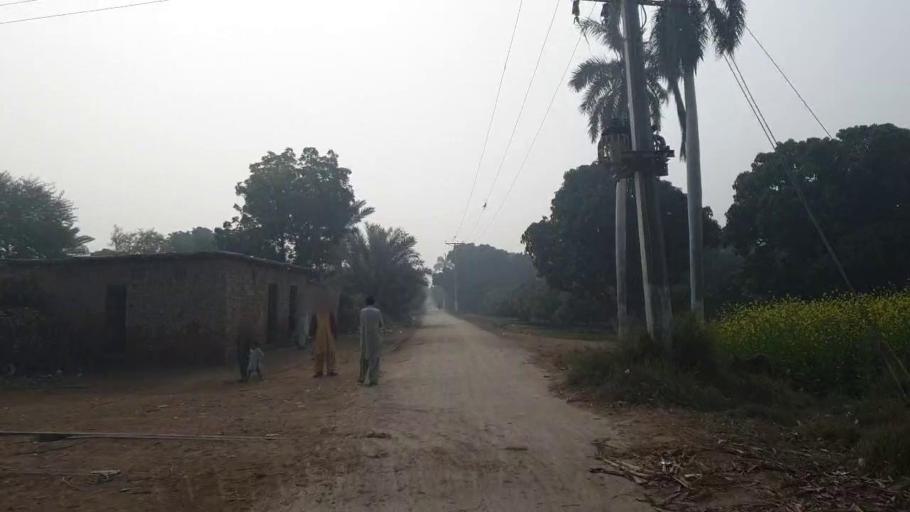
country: PK
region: Sindh
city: Tando Adam
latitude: 25.7900
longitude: 68.5962
